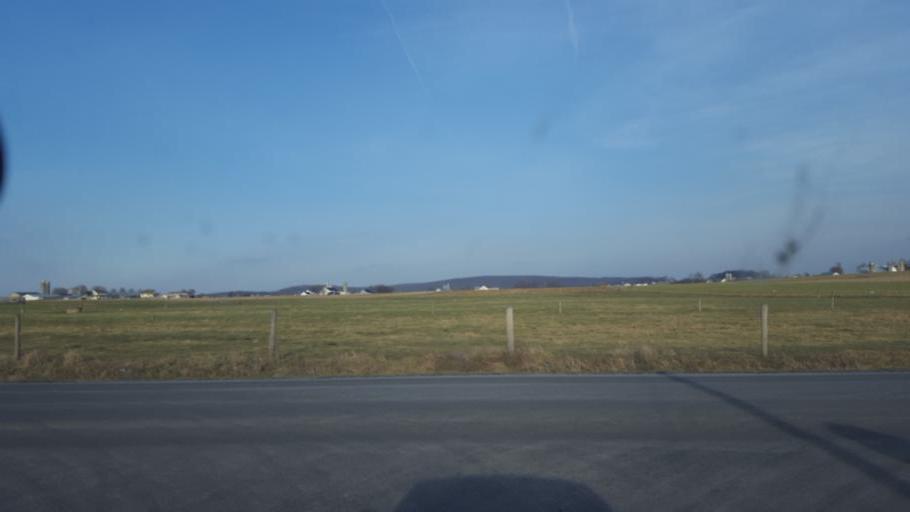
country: US
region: Pennsylvania
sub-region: Lancaster County
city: Intercourse
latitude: 40.0588
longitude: -76.1036
